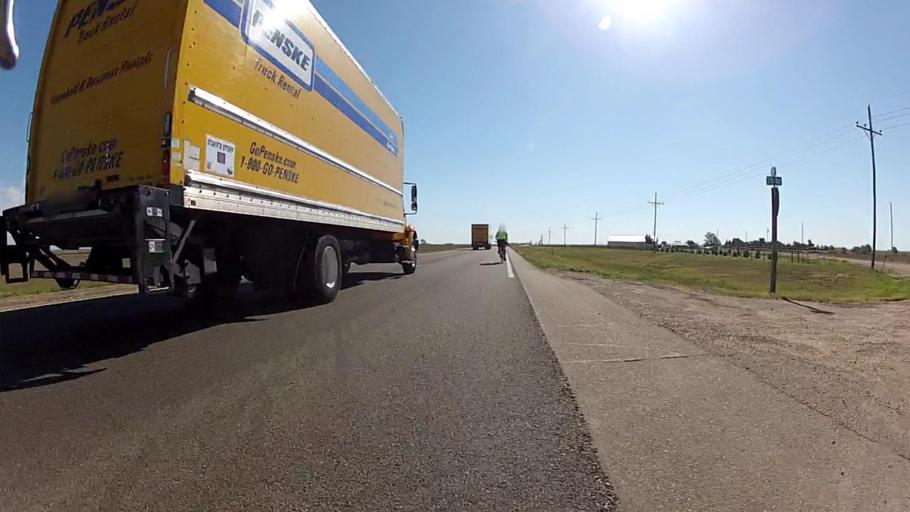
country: US
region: Kansas
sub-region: Gray County
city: Cimarron
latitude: 37.5772
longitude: -100.5209
